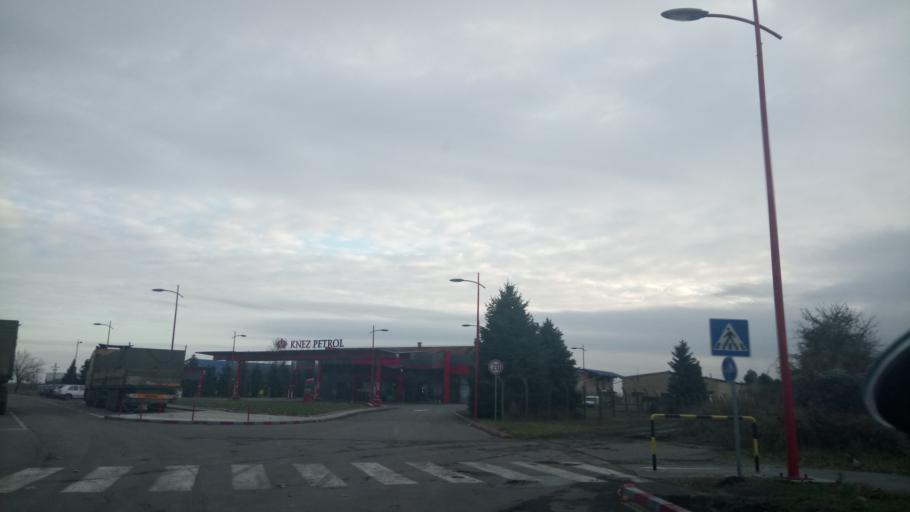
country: RS
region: Autonomna Pokrajina Vojvodina
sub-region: Sremski Okrug
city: Stara Pazova
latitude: 44.9688
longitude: 20.1801
